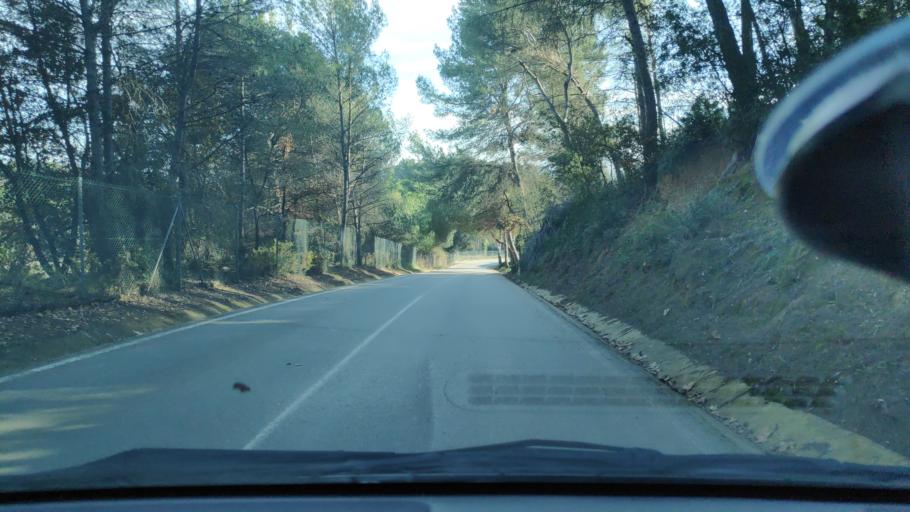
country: ES
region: Catalonia
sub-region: Provincia de Barcelona
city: Rubi
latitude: 41.4977
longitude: 2.0573
